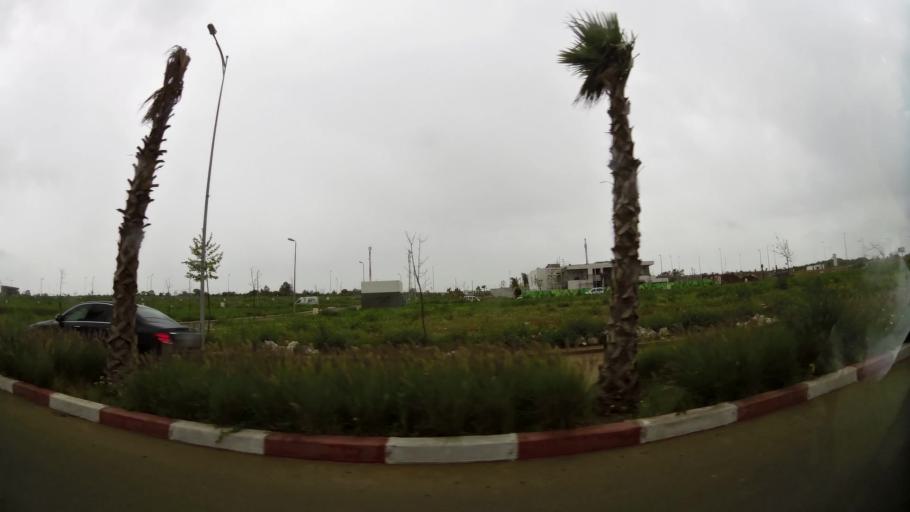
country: MA
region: Grand Casablanca
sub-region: Casablanca
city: Casablanca
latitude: 33.5223
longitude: -7.6277
